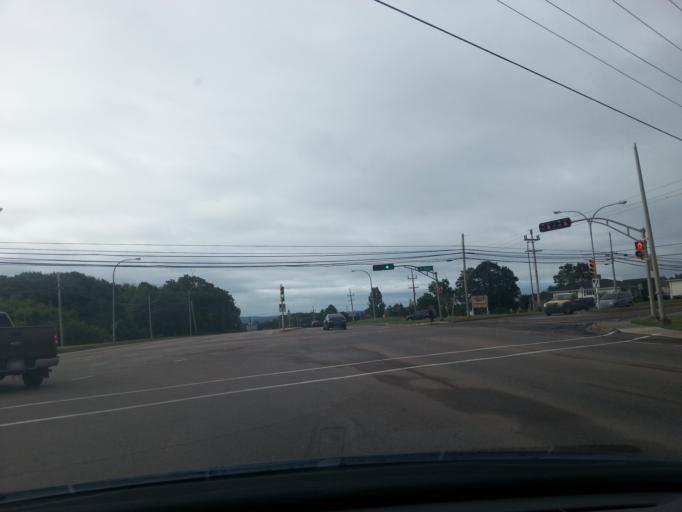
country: CA
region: Prince Edward Island
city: Charlottetown
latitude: 46.2689
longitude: -63.1140
